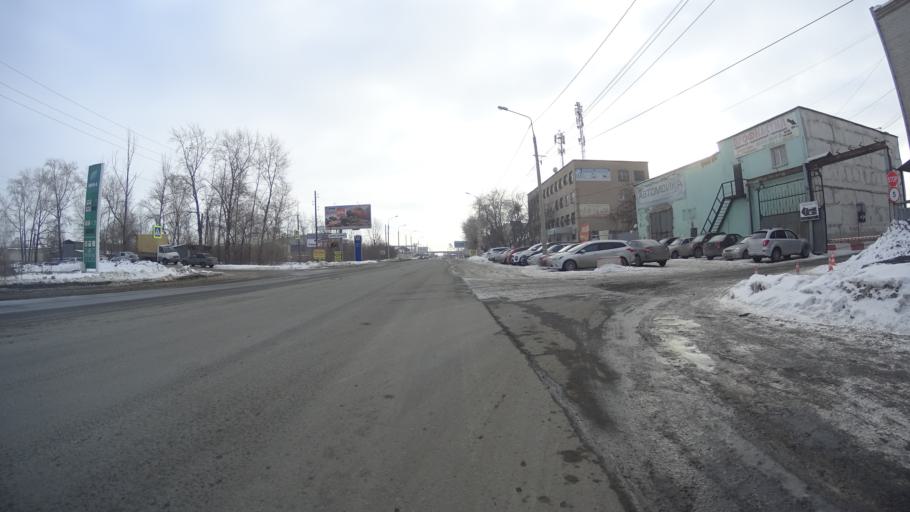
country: RU
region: Chelyabinsk
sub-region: Gorod Chelyabinsk
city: Chelyabinsk
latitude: 55.1232
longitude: 61.3859
